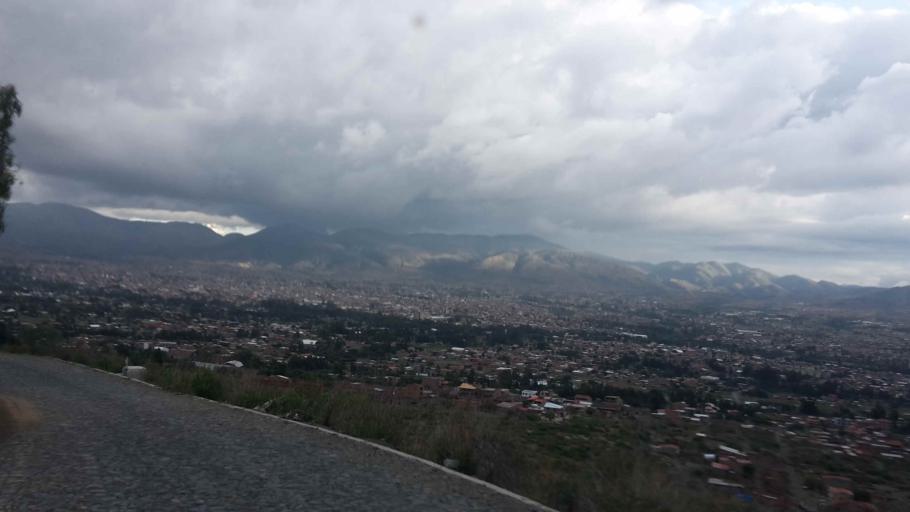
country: BO
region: Cochabamba
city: Cochabamba
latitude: -17.3716
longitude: -66.0632
